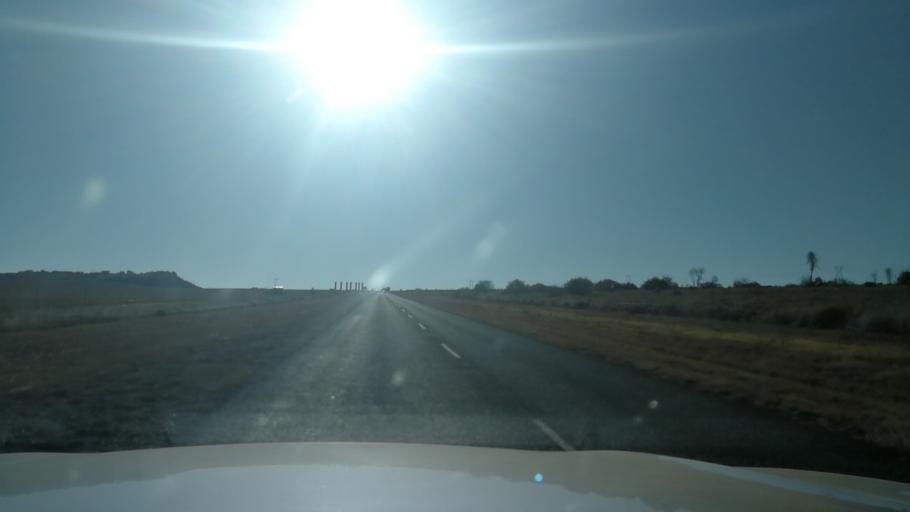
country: ZA
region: Gauteng
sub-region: West Rand District Municipality
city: Krugersdorp
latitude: -25.9833
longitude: 27.6573
